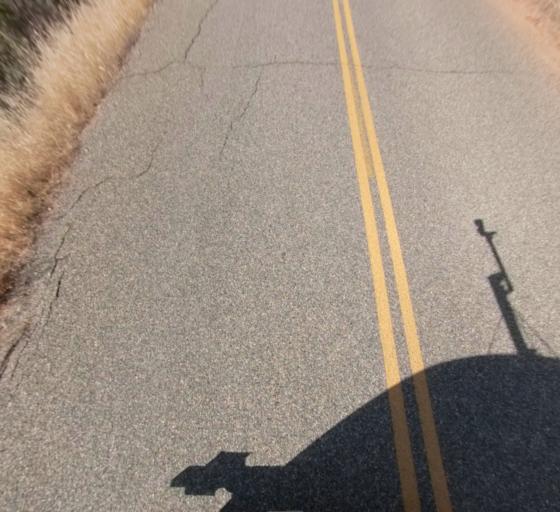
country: US
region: California
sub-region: Fresno County
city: Auberry
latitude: 37.1833
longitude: -119.4280
